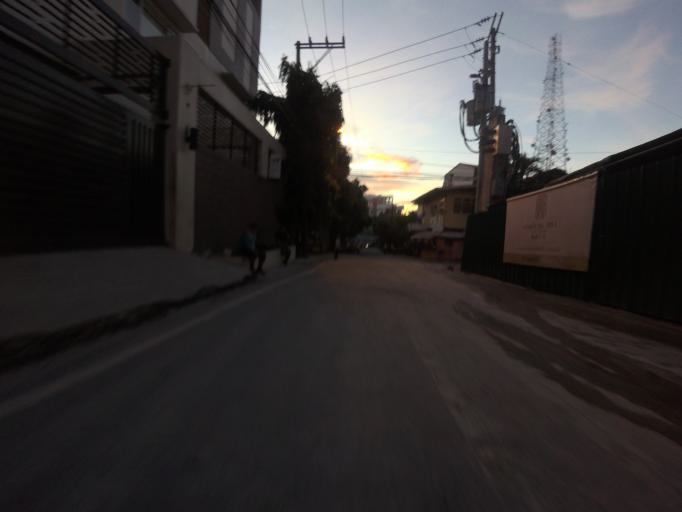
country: PH
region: Metro Manila
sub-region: San Juan
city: San Juan
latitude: 14.5932
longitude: 121.0388
